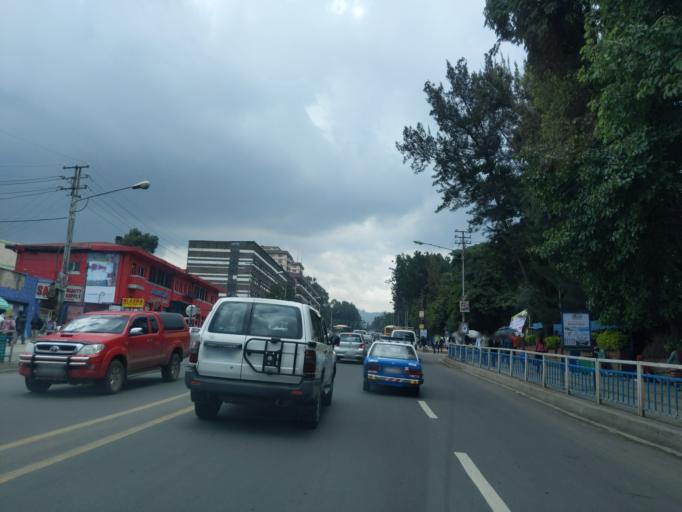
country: ET
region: Adis Abeba
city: Addis Ababa
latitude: 9.0335
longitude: 38.7634
